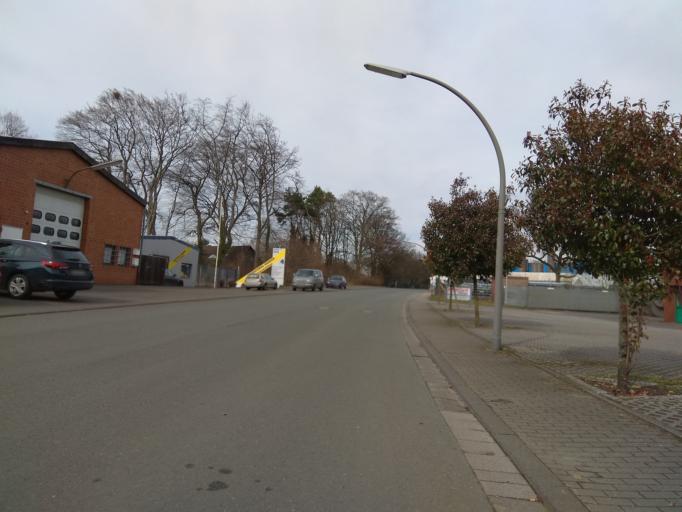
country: DE
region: North Rhine-Westphalia
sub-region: Regierungsbezirk Munster
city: Recklinghausen
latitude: 51.6710
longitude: 7.1615
